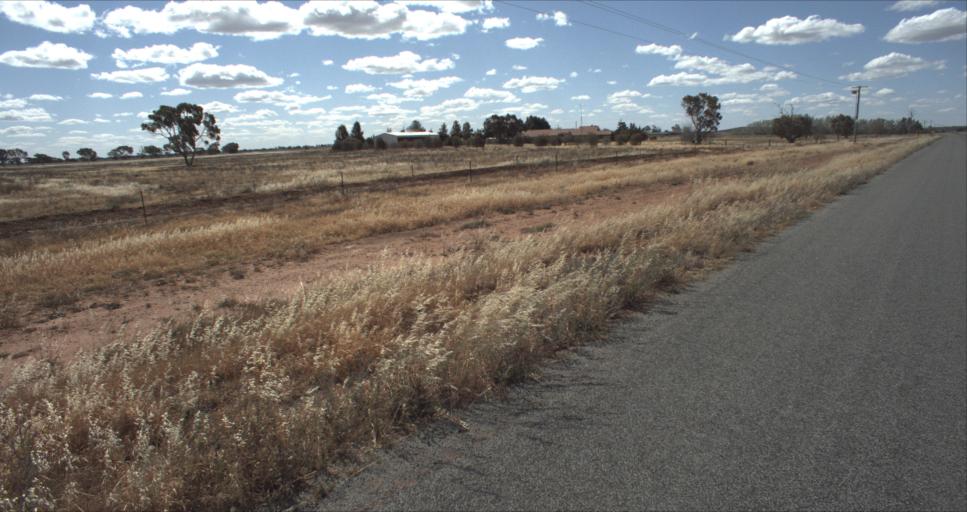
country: AU
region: New South Wales
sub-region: Leeton
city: Leeton
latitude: -34.4619
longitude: 146.2526
